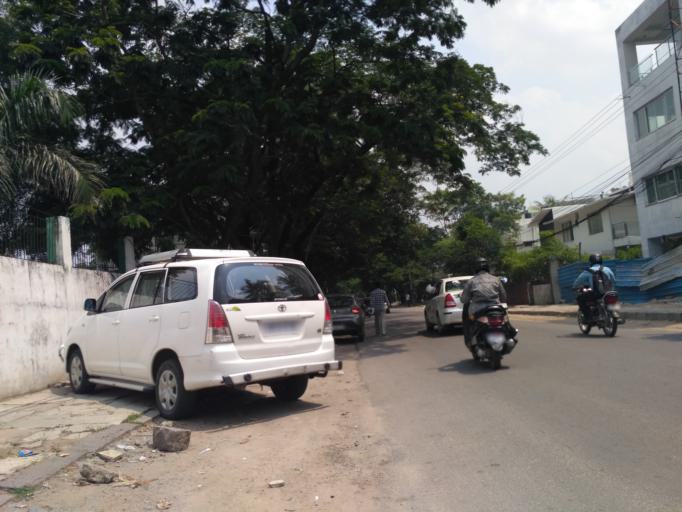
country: IN
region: Telangana
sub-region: Rangareddi
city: Kukatpalli
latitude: 17.4293
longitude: 78.4140
